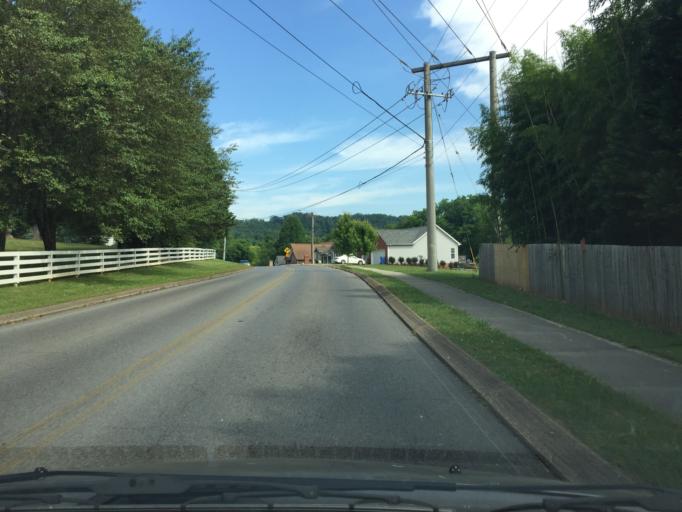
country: US
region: Tennessee
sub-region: Hamilton County
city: Collegedale
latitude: 35.0650
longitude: -85.0362
